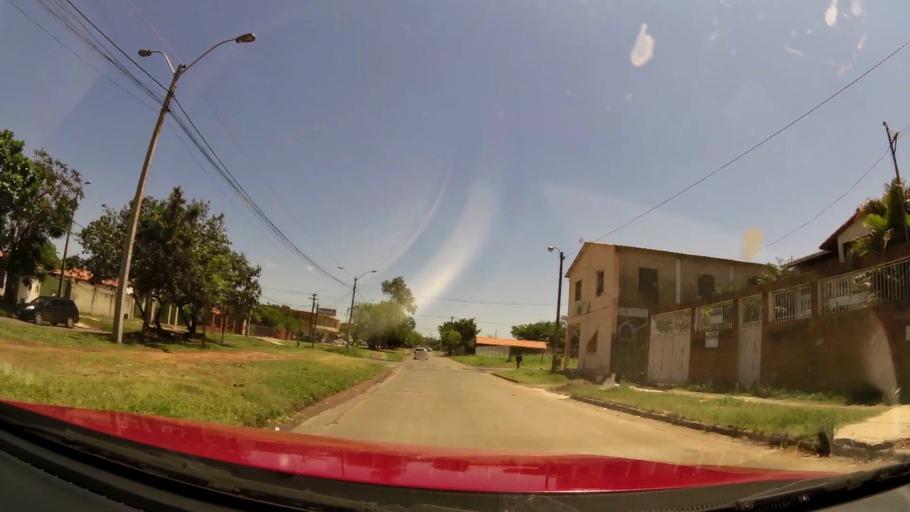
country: PY
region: Central
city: Colonia Mariano Roque Alonso
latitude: -25.2336
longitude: -57.5474
